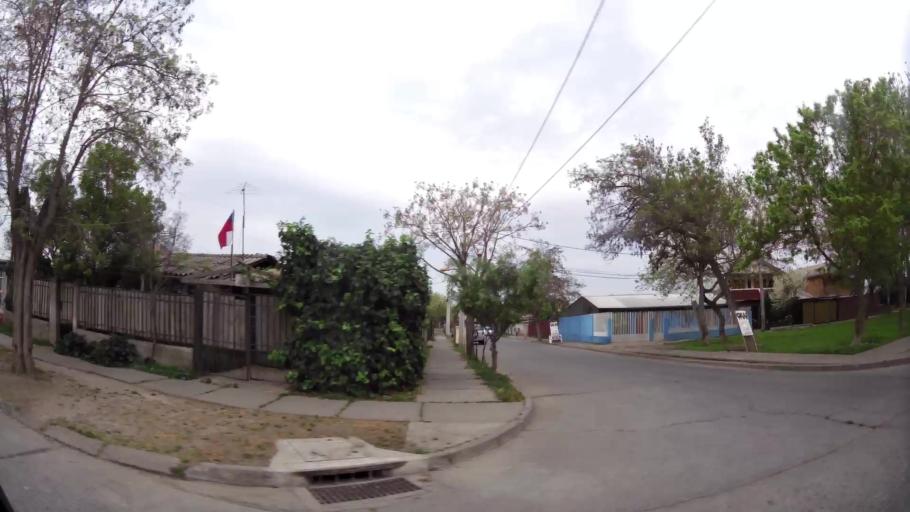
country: CL
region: Santiago Metropolitan
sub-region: Provincia de Santiago
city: Lo Prado
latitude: -33.4997
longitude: -70.7716
